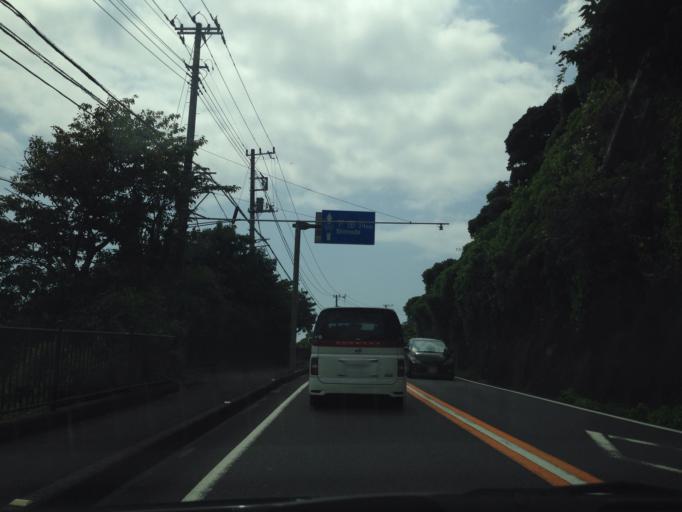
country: JP
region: Shizuoka
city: Shimoda
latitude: 34.7393
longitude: 138.9991
